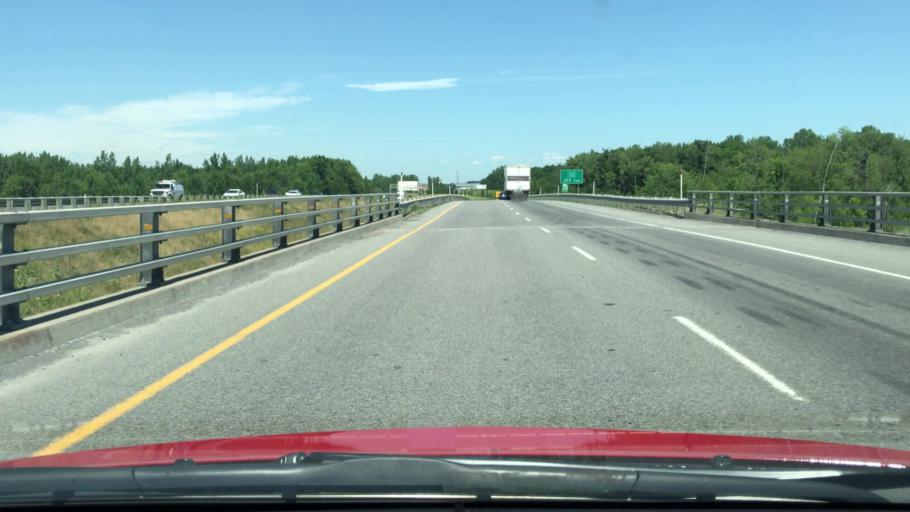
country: CA
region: Quebec
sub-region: Monteregie
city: Saint-Constant
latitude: 45.3854
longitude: -73.6084
